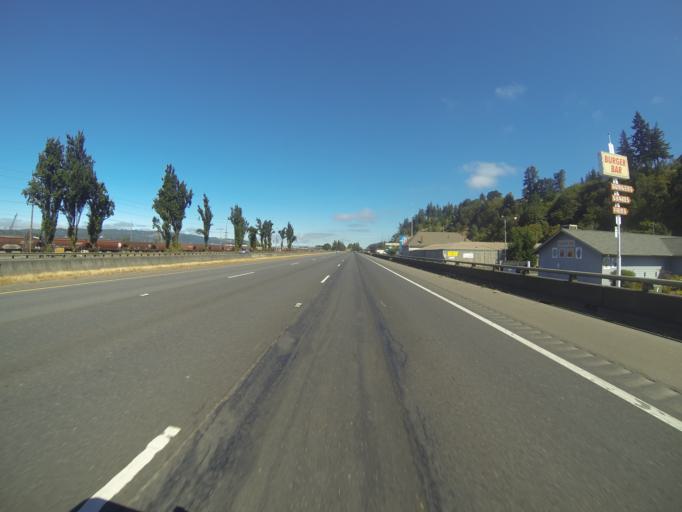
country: US
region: Washington
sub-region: Cowlitz County
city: Kalama
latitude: 46.0116
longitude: -122.8471
